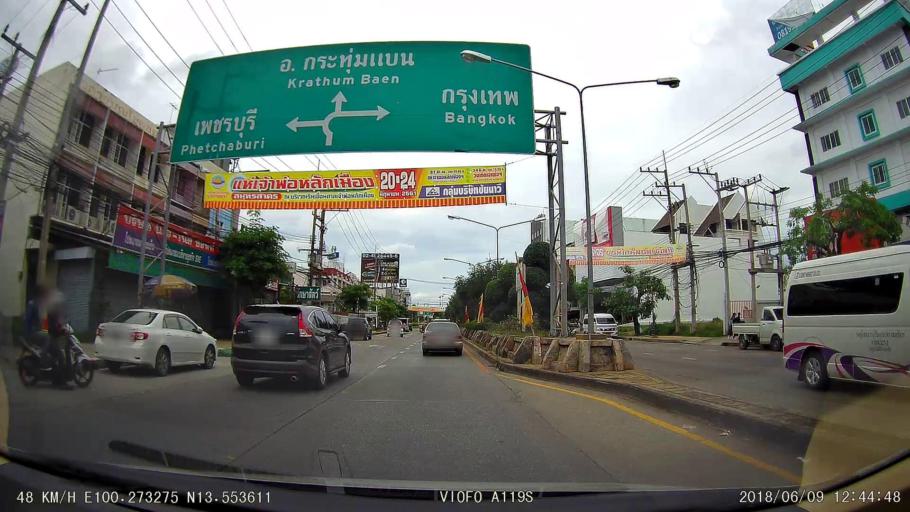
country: TH
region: Samut Sakhon
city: Samut Sakhon
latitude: 13.5551
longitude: 100.2721
